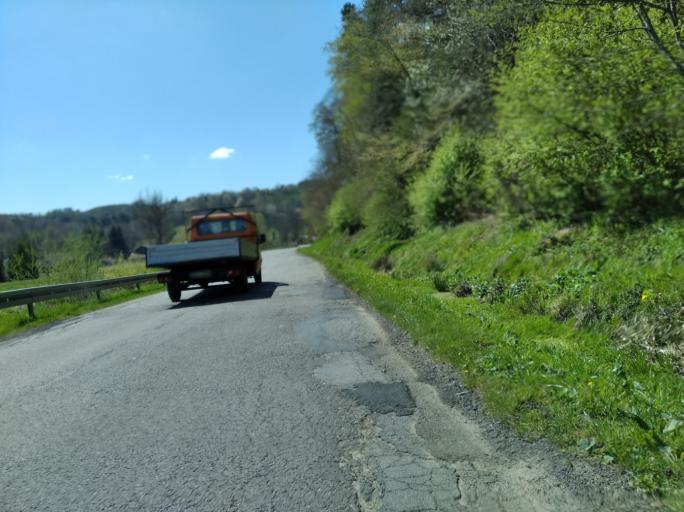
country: PL
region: Subcarpathian Voivodeship
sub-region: Powiat brzozowski
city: Dydnia
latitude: 49.6999
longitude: 22.1930
